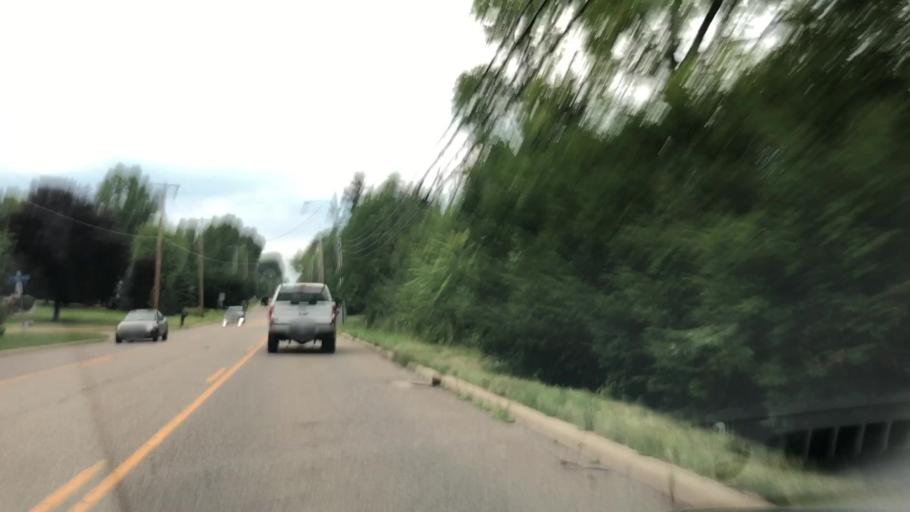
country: US
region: Ohio
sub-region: Stark County
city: Perry Heights
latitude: 40.8024
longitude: -81.4842
